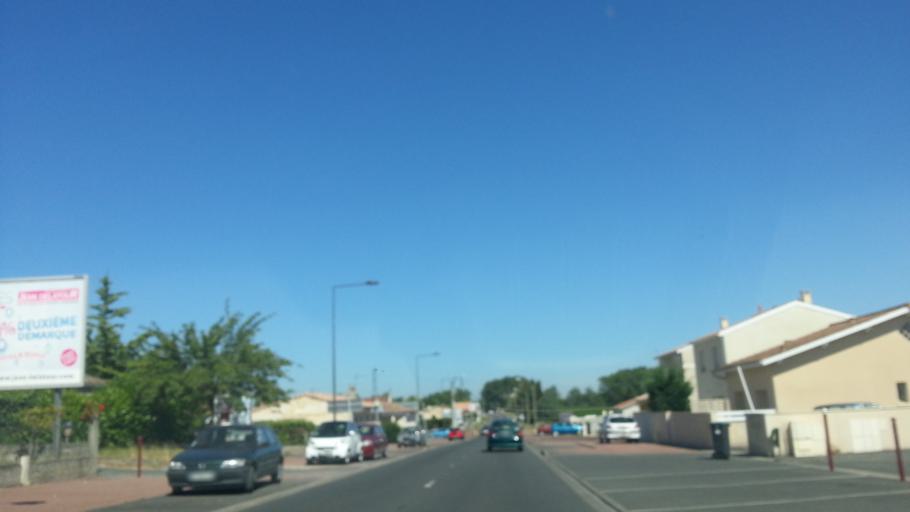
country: FR
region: Aquitaine
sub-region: Departement de la Gironde
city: Cadaujac
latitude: 44.7524
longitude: -0.5494
